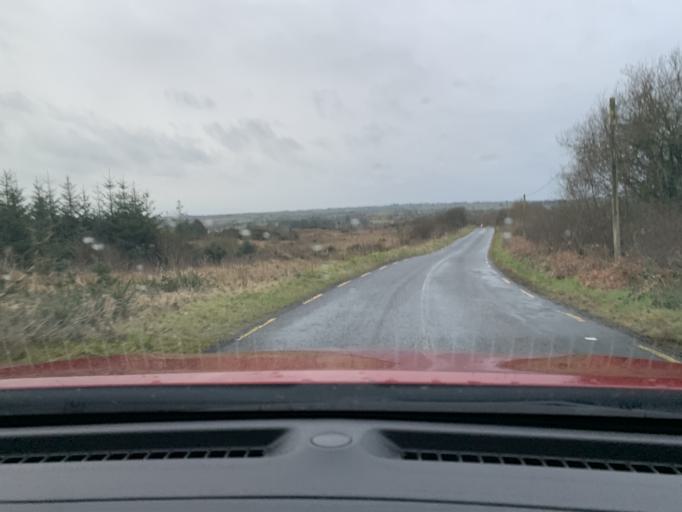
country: IE
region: Connaught
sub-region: Roscommon
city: Boyle
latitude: 53.9833
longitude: -8.3385
